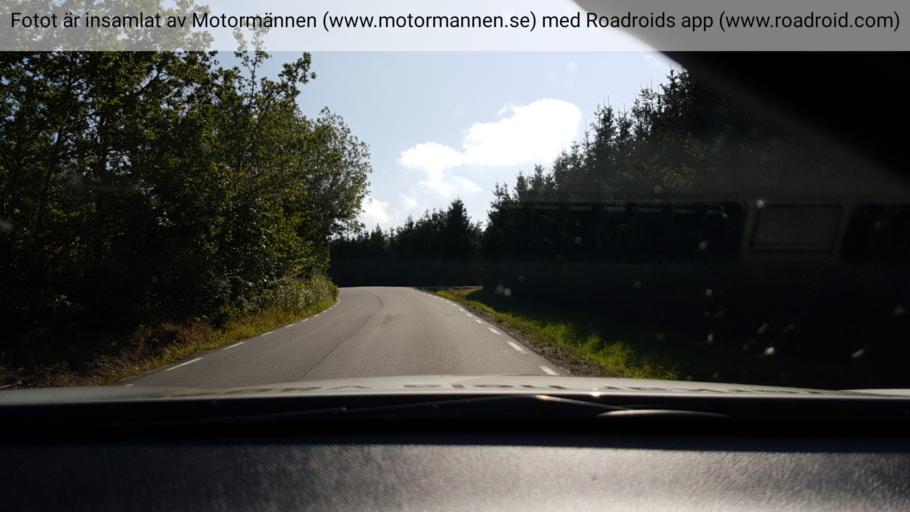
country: SE
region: Stockholm
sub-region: Nynashamns Kommun
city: Osmo
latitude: 58.8942
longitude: 17.8402
